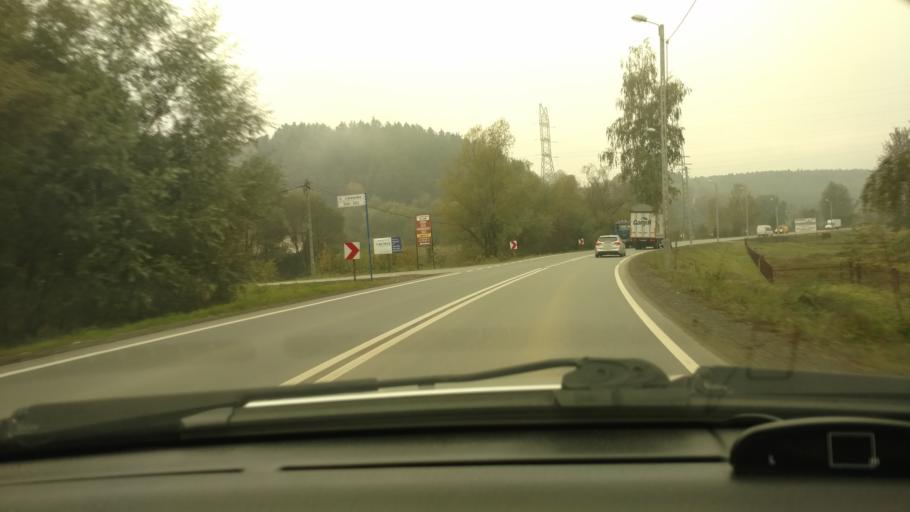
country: PL
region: Lesser Poland Voivodeship
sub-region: Powiat nowosadecki
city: Nawojowa
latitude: 49.6072
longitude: 20.7568
